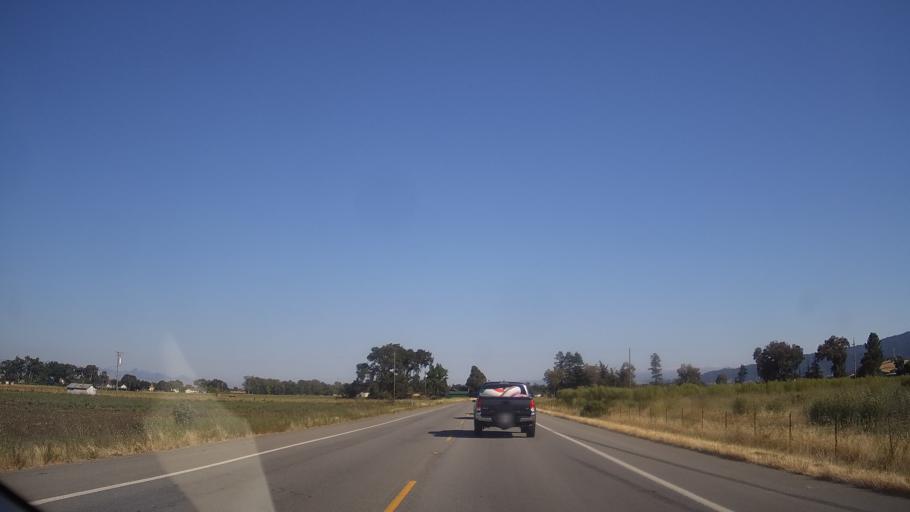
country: US
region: California
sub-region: Santa Clara County
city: San Martin
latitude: 37.0612
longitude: -121.6099
